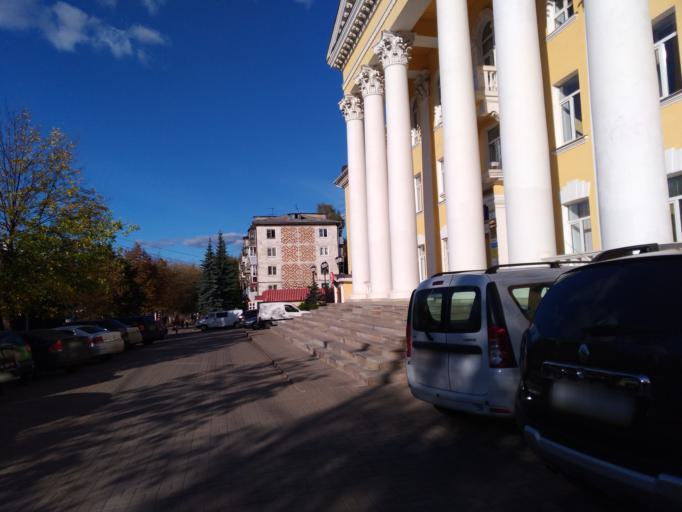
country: RU
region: Kaluga
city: Kaluga
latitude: 54.5217
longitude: 36.2696
